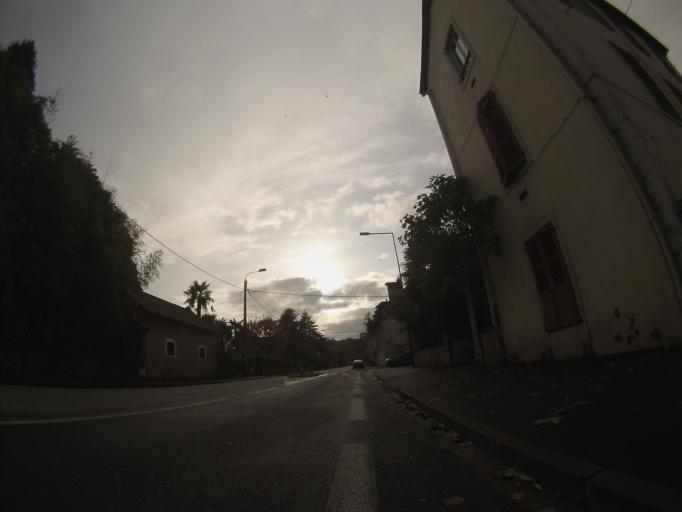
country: FR
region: Aquitaine
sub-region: Departement des Pyrenees-Atlantiques
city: Jurancon
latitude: 43.2868
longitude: -0.3812
